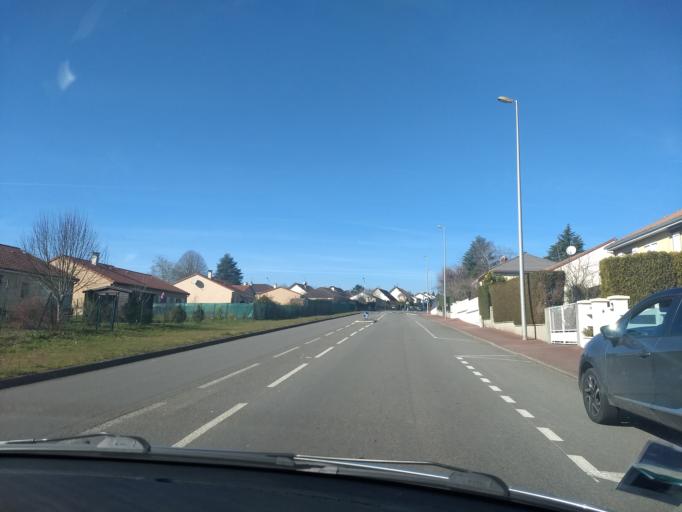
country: FR
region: Limousin
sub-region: Departement de la Haute-Vienne
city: Isle
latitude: 45.8239
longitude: 1.2062
